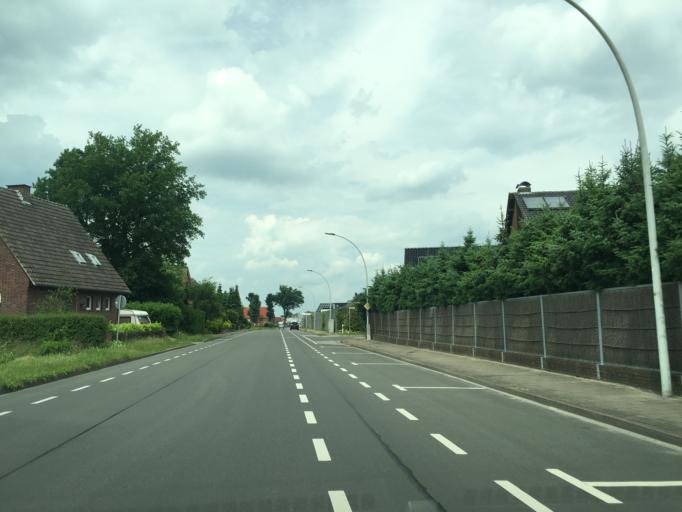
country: DE
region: North Rhine-Westphalia
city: Emsdetten
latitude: 52.1710
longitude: 7.5019
